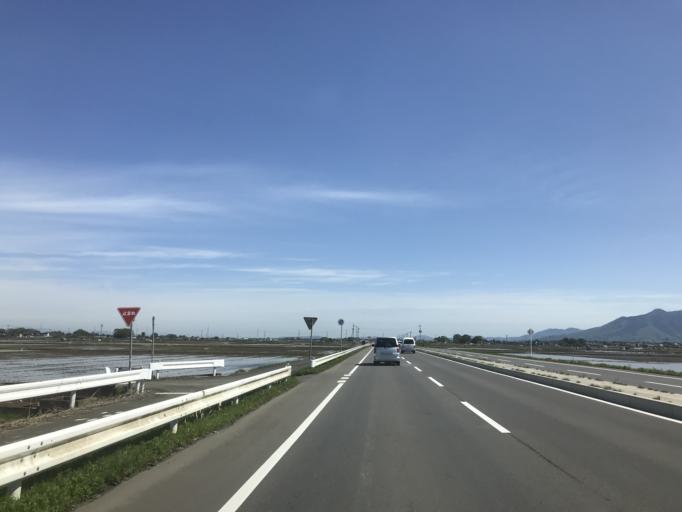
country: JP
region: Ibaraki
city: Ishige
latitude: 36.1351
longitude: 139.9850
